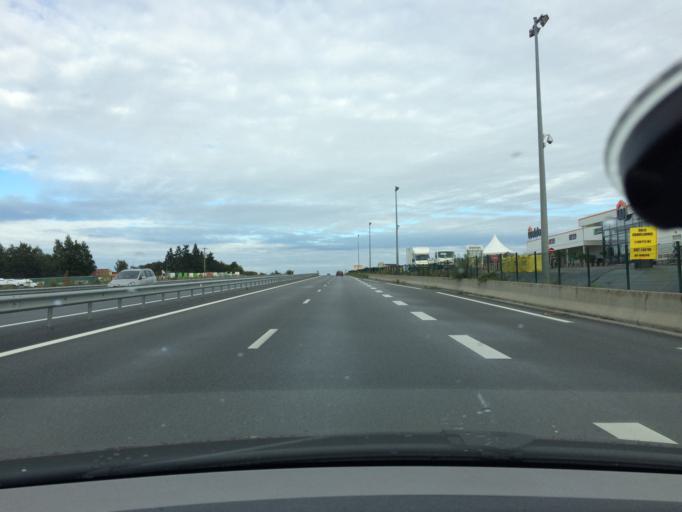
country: FR
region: Brittany
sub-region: Departement d'Ille-et-Vilaine
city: Corps-Nuds
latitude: 47.9727
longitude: -1.5409
